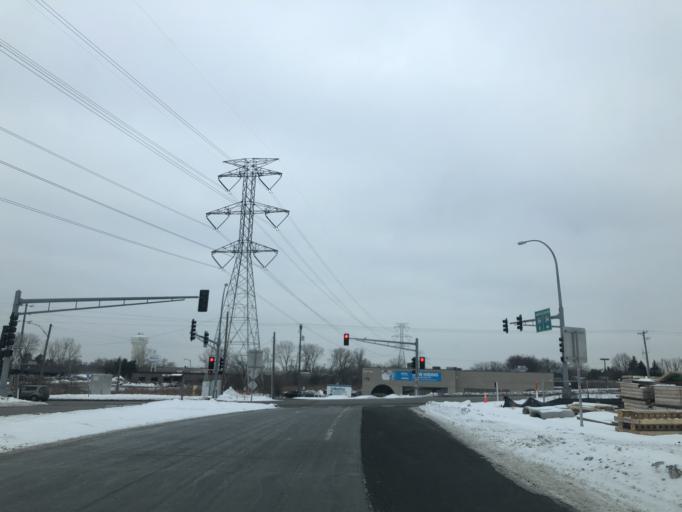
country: US
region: Minnesota
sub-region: Hennepin County
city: Saint Anthony
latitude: 45.0350
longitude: -93.1923
